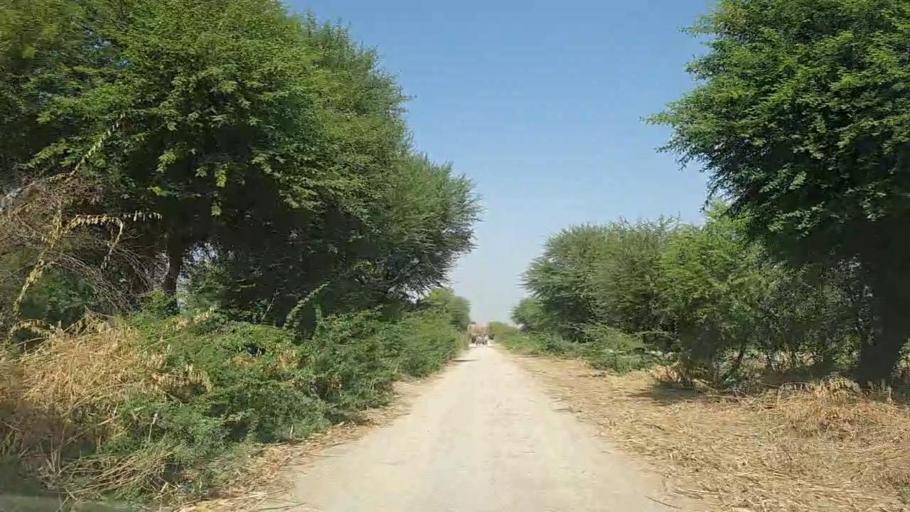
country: PK
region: Sindh
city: Samaro
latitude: 25.1849
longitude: 69.4040
